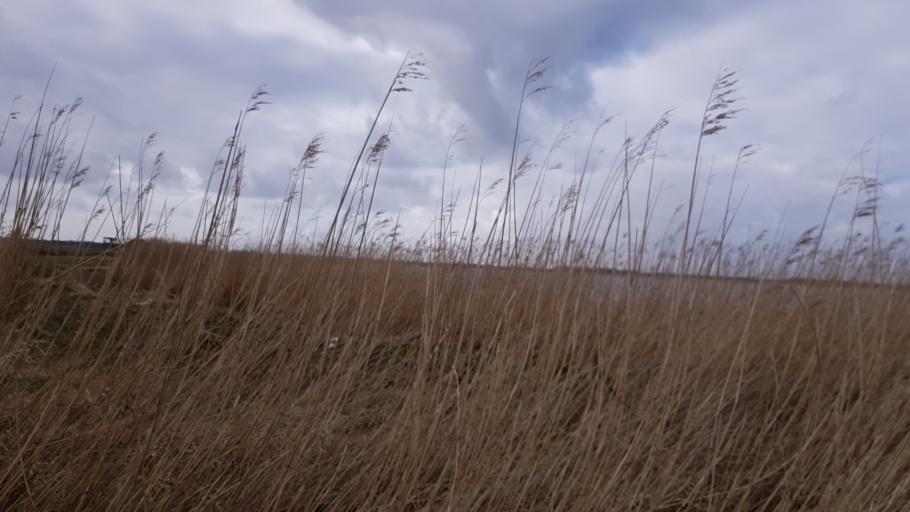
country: NL
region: Utrecht
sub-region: Gemeente Bunschoten
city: Spakenburg
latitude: 52.2763
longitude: 5.3083
